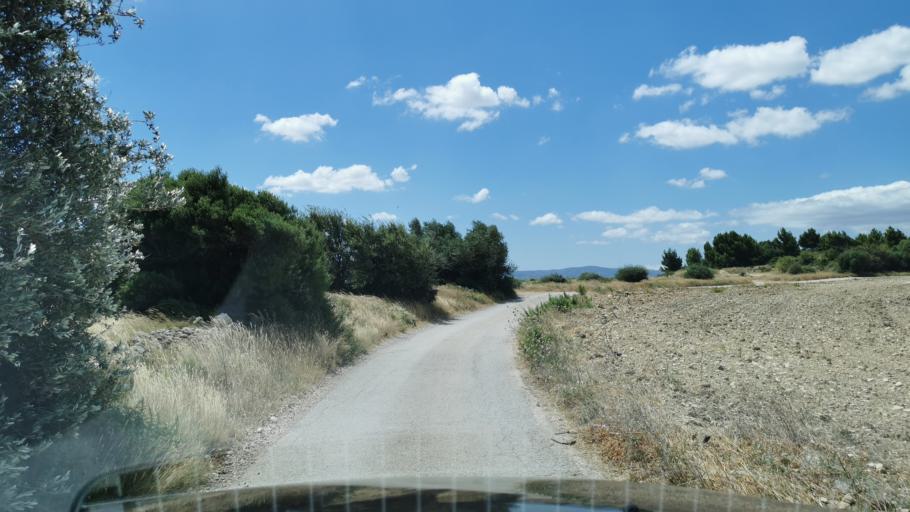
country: FR
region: Languedoc-Roussillon
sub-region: Departement de l'Aude
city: Peyriac-de-Mer
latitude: 43.0903
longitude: 2.9828
